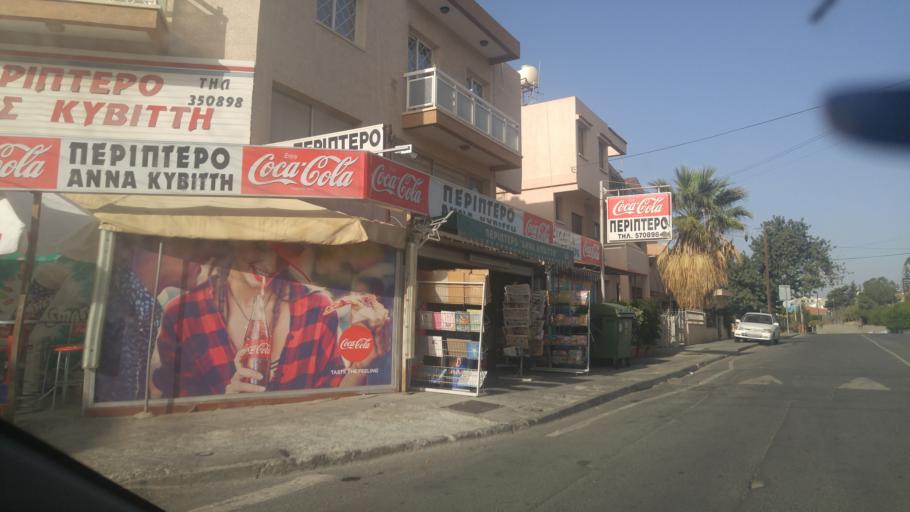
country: CY
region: Limassol
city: Limassol
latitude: 34.6828
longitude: 33.0097
